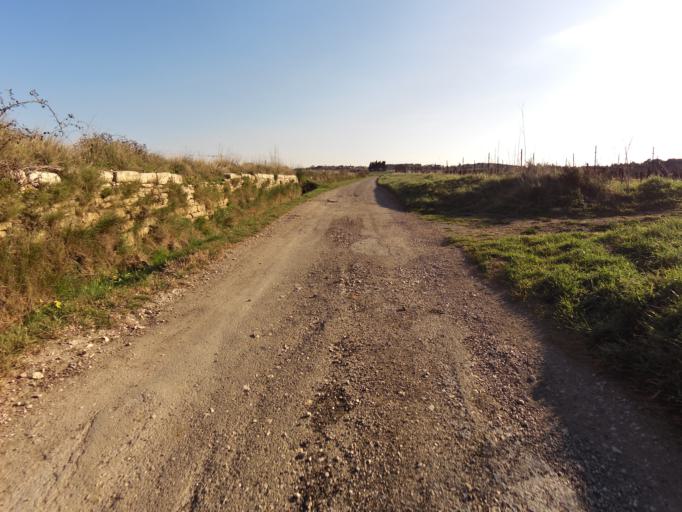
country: FR
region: Languedoc-Roussillon
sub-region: Departement du Gard
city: Aigues-Vives
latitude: 43.7512
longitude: 4.1804
